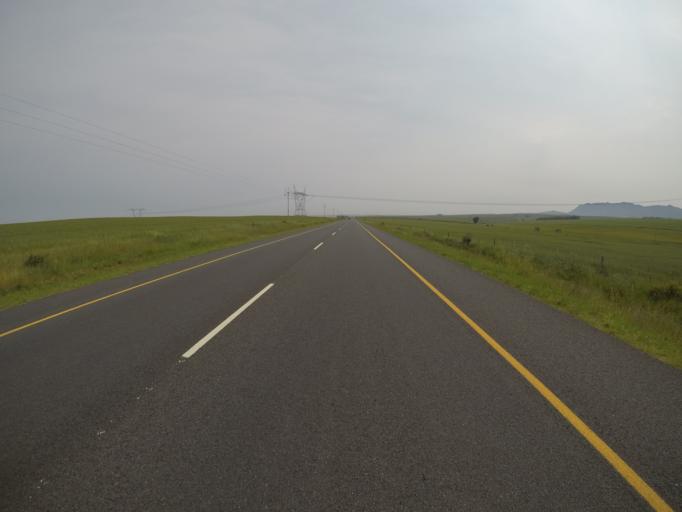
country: ZA
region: Western Cape
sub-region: West Coast District Municipality
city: Malmesbury
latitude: -33.4939
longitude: 18.8274
